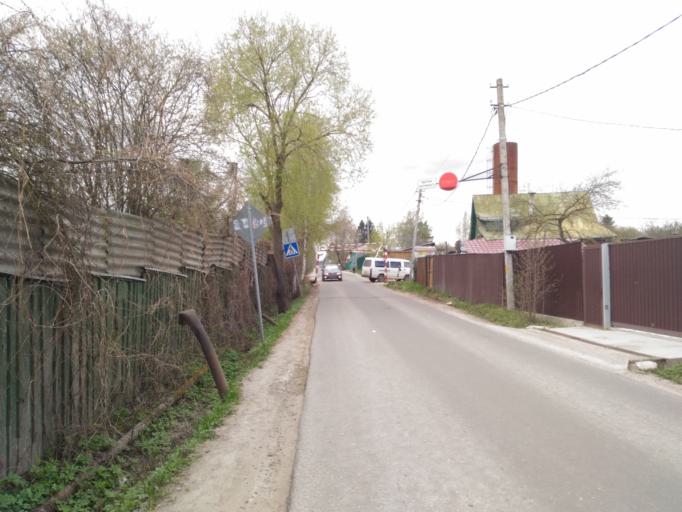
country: RU
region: Moskovskaya
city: Nakhabino
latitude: 55.8502
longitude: 37.1472
